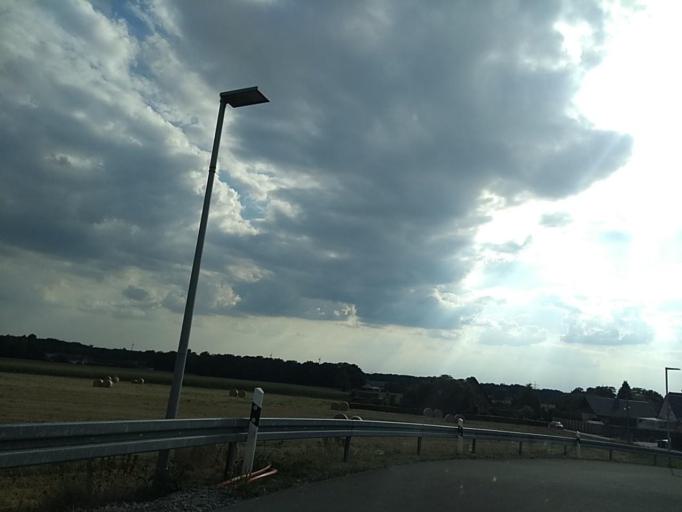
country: DE
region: North Rhine-Westphalia
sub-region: Regierungsbezirk Detmold
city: Verl
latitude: 51.9414
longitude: 8.5340
